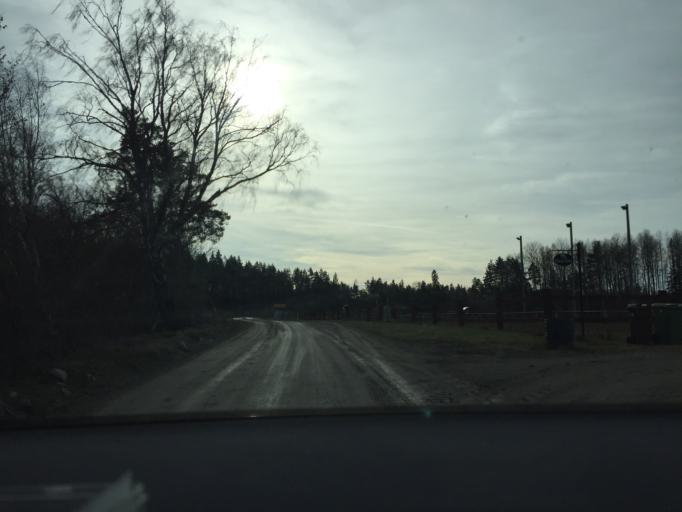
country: SE
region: OErebro
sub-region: Orebro Kommun
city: Odensbacken
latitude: 59.1326
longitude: 15.4756
